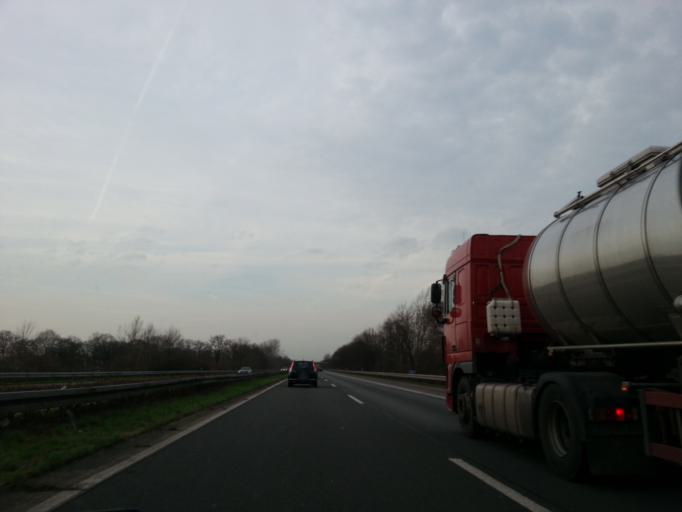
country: DE
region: North Rhine-Westphalia
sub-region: Regierungsbezirk Dusseldorf
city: Hamminkeln
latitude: 51.7567
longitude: 6.5606
